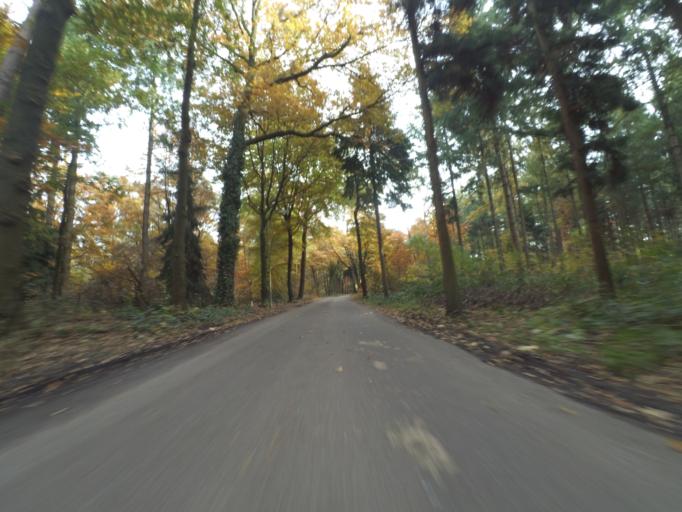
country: NL
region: Gelderland
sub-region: Gemeente Ede
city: Lunteren
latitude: 52.0841
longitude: 5.6368
